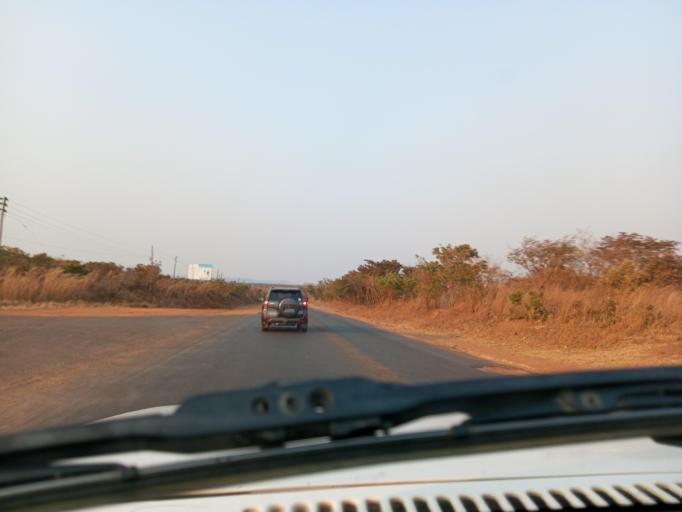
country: ZM
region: Northern
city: Mpika
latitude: -11.8938
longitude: 31.4174
